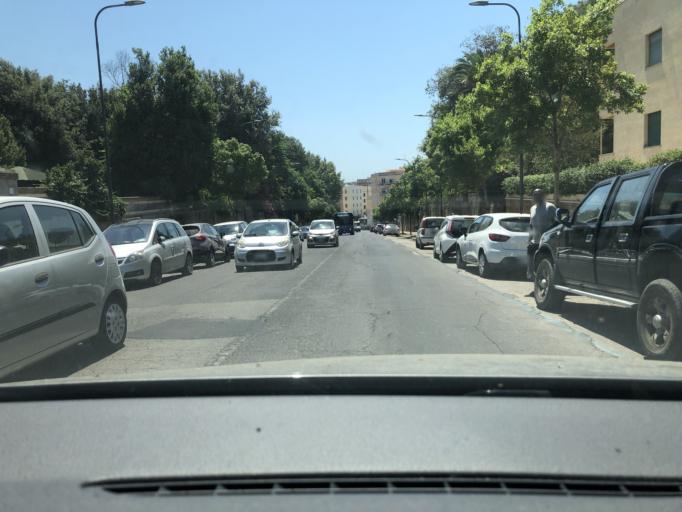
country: IT
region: Latium
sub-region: Citta metropolitana di Roma Capitale
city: Anzio
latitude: 41.4503
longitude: 12.6298
